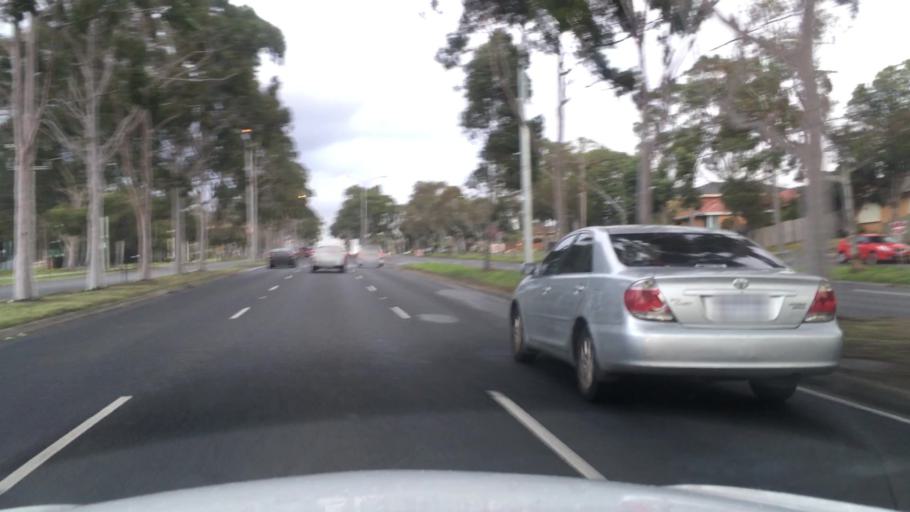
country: AU
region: Victoria
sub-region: Monash
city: Notting Hill
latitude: -37.9143
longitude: 145.1594
